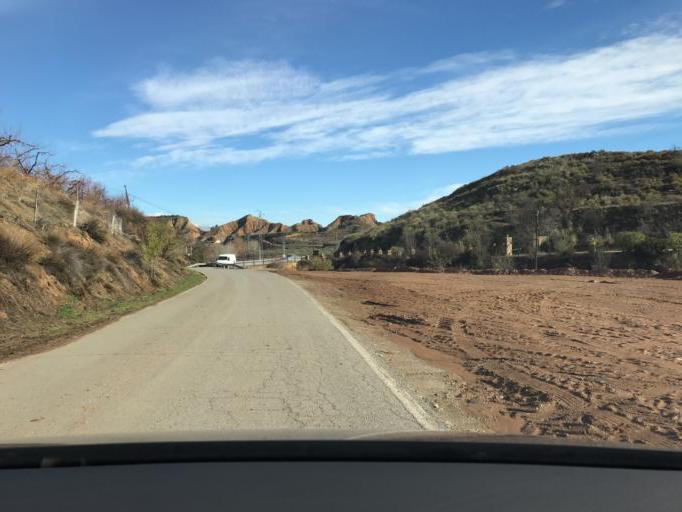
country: ES
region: Andalusia
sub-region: Provincia de Granada
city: Marchal
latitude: 37.2939
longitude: -3.2269
